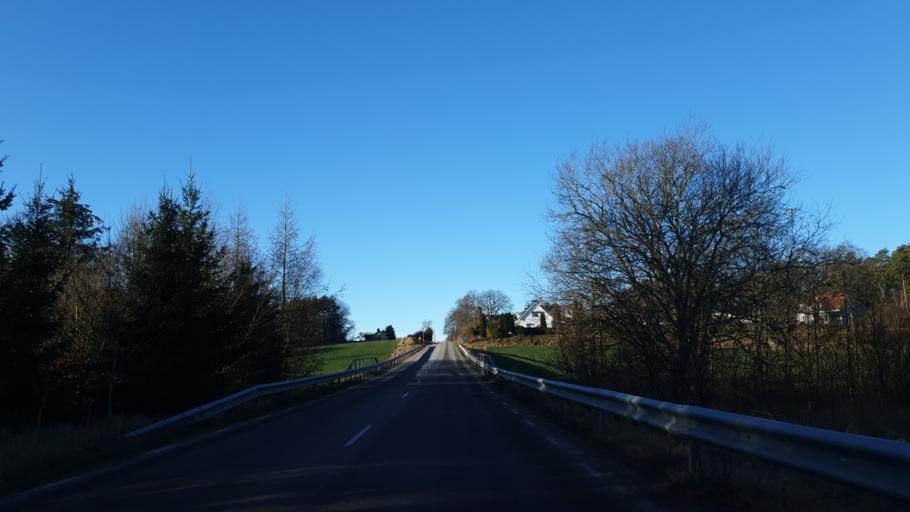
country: SE
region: Blekinge
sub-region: Ronneby Kommun
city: Ronneby
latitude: 56.1960
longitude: 15.3364
